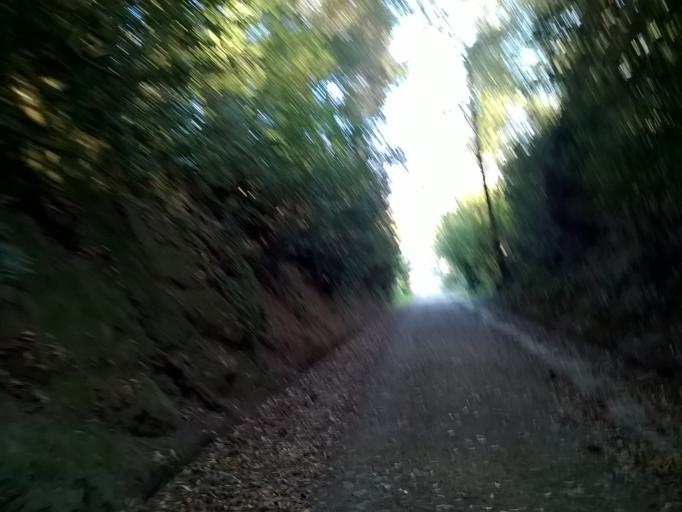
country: FR
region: Pays de la Loire
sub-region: Departement de la Loire-Atlantique
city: Nantes
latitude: 47.1997
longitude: -1.5846
